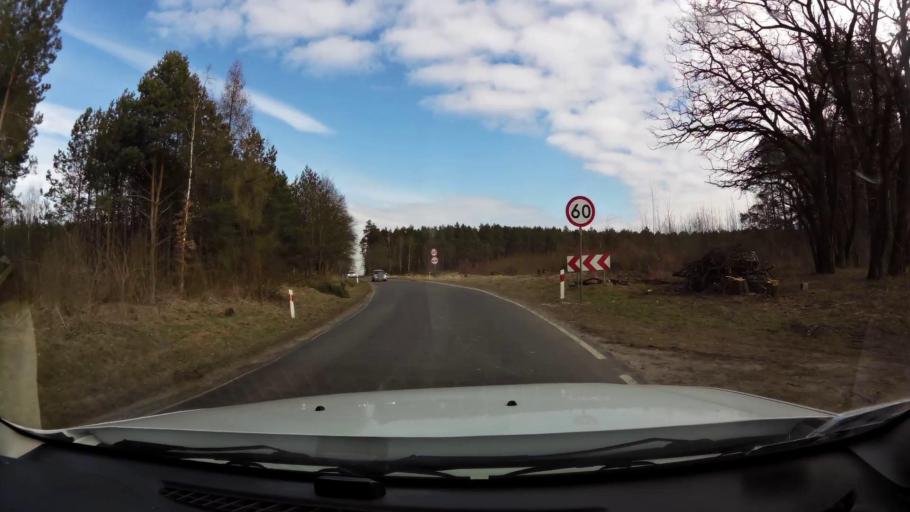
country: PL
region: West Pomeranian Voivodeship
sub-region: Powiat mysliborski
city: Debno
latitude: 52.7200
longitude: 14.6818
